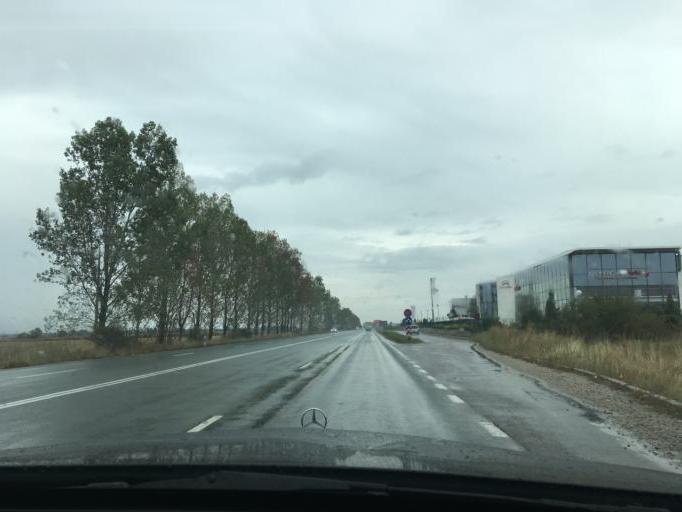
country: BG
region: Sofiya
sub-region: Obshtina Bozhurishte
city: Bozhurishte
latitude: 42.7741
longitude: 23.1870
